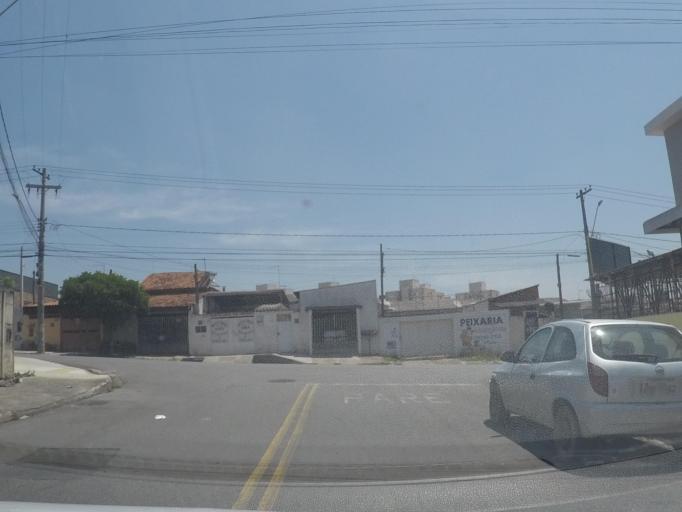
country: BR
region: Sao Paulo
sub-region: Hortolandia
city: Hortolandia
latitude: -22.8591
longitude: -47.2017
